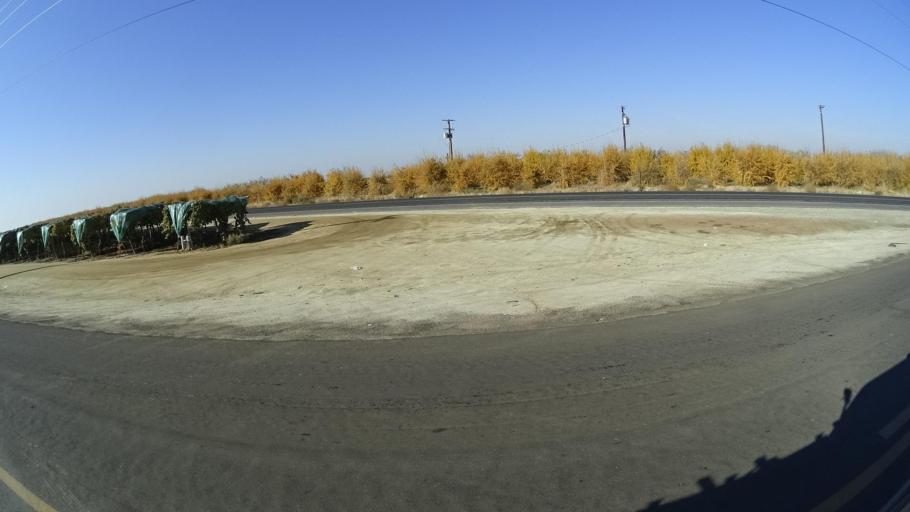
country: US
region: California
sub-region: Tulare County
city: Richgrove
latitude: 35.7582
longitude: -119.1341
